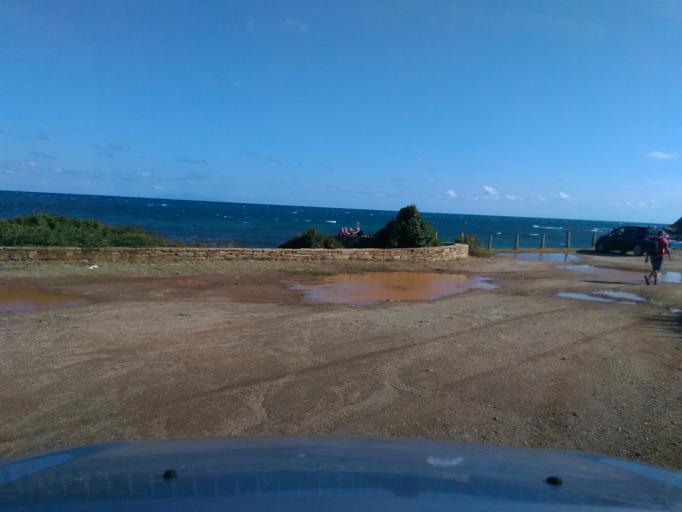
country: FR
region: Corsica
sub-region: Departement de la Haute-Corse
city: Brando
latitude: 42.9743
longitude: 9.4539
